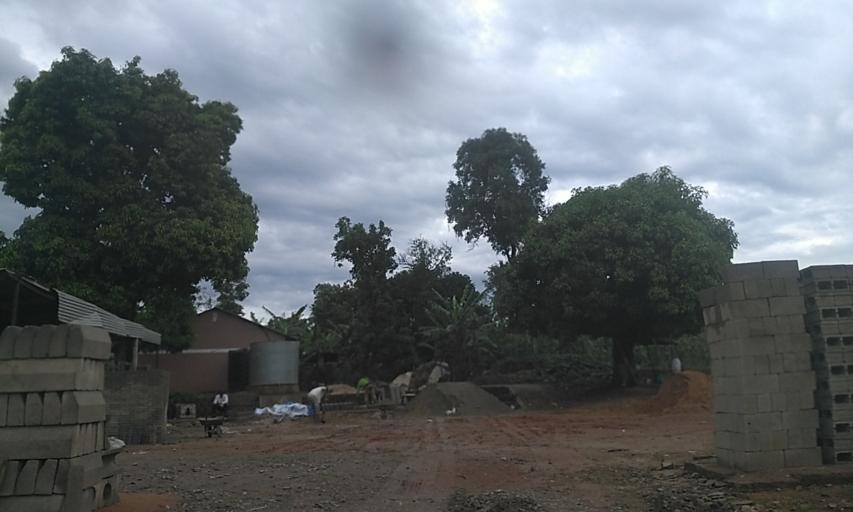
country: UG
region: Central Region
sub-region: Wakiso District
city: Bweyogerere
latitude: 0.3931
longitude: 32.6619
